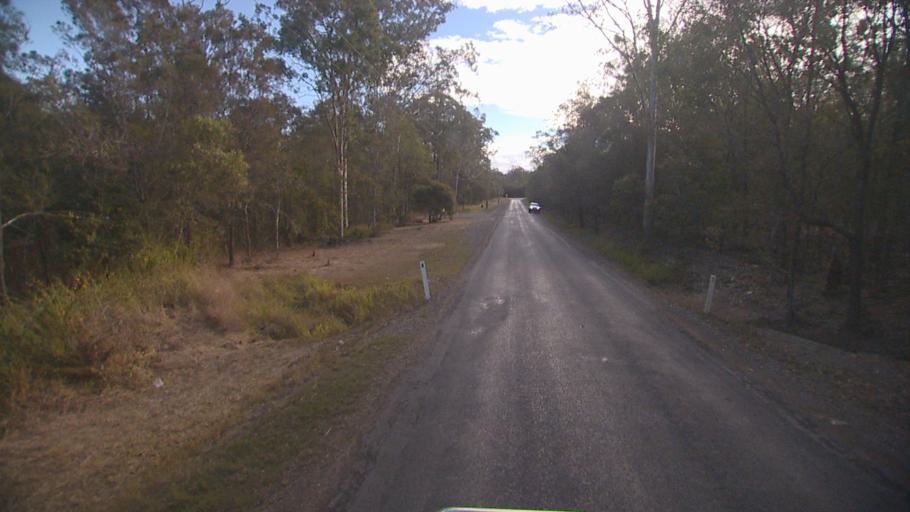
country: AU
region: Queensland
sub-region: Logan
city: Cedar Vale
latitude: -27.8335
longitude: 153.0554
